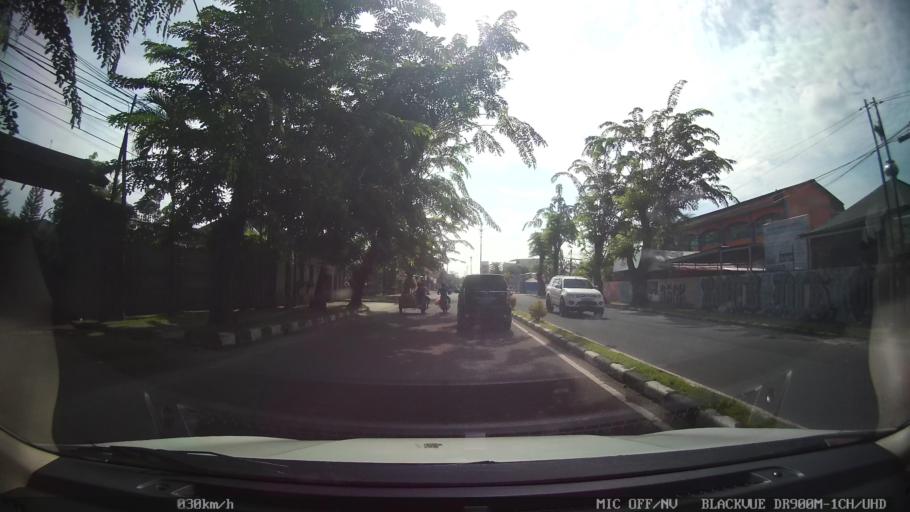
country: ID
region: North Sumatra
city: Medan
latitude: 3.5676
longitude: 98.6478
